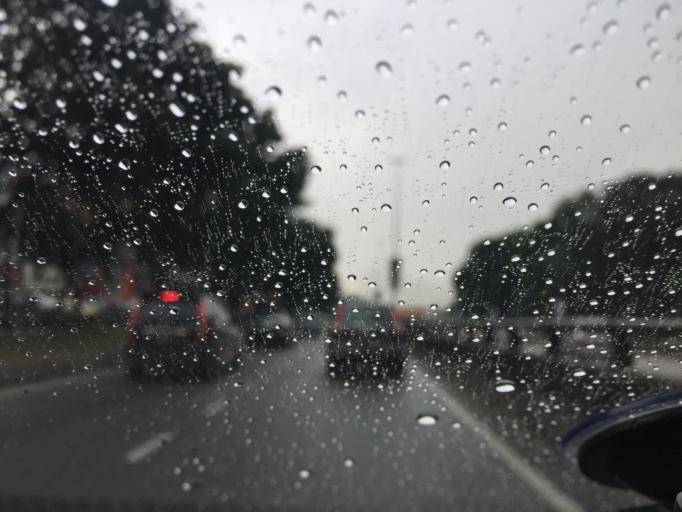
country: MY
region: Selangor
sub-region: Petaling
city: Petaling Jaya
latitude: 3.0744
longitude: 101.6109
